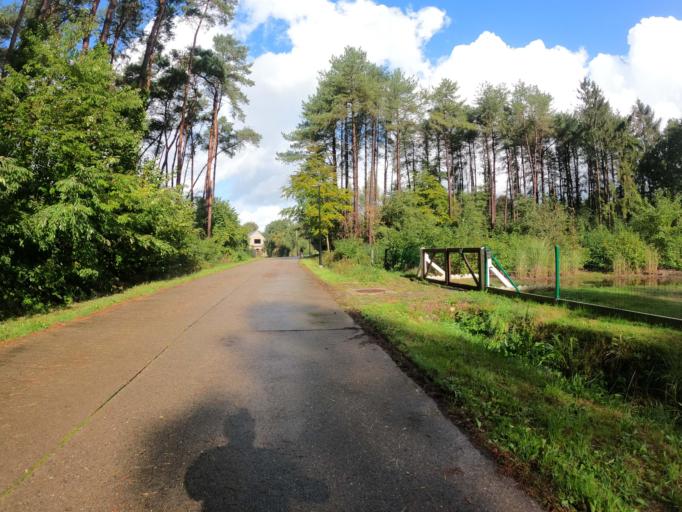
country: BE
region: Flanders
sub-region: Provincie Antwerpen
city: Lille
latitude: 51.2288
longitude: 4.8098
